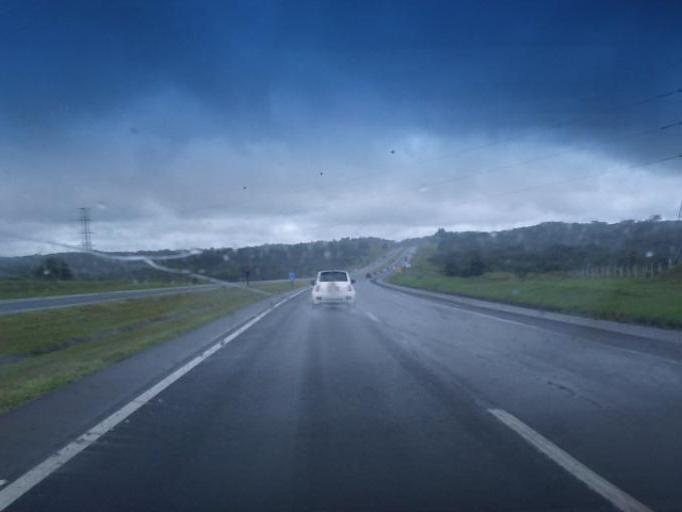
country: BR
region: Parana
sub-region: Piraquara
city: Piraquara
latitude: -25.4831
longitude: -49.1067
